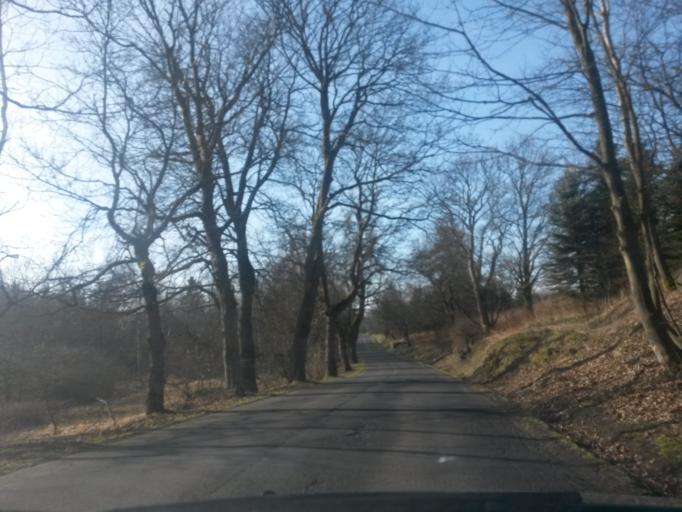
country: CZ
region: Ustecky
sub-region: Okres Chomutov
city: Perstejn
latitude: 50.4499
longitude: 13.1331
